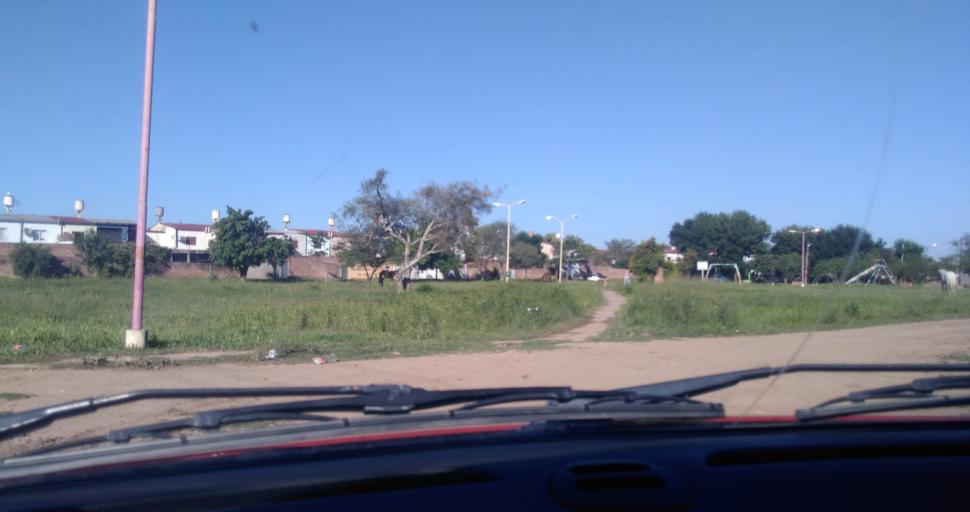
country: AR
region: Chaco
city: Resistencia
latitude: -27.4408
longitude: -58.9611
